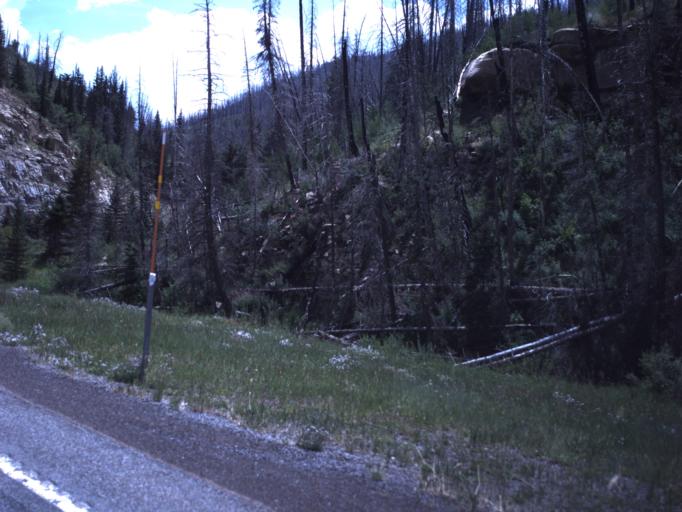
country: US
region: Utah
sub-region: Sanpete County
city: Fairview
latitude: 39.5884
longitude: -111.1936
